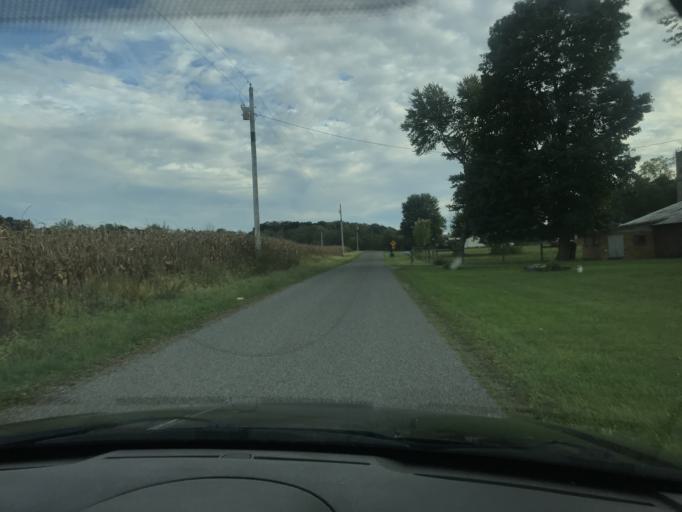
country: US
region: Ohio
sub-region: Logan County
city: West Liberty
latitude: 40.2496
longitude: -83.6950
